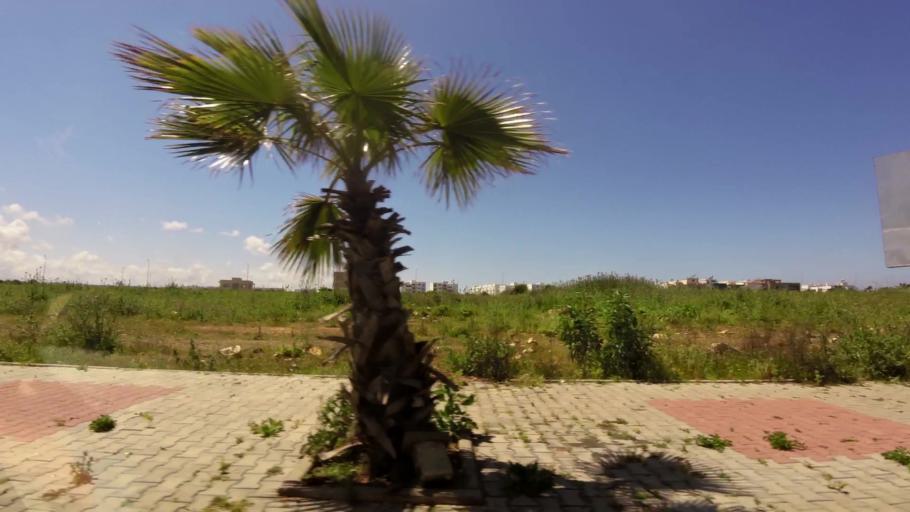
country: MA
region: Grand Casablanca
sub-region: Nouaceur
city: Dar Bouazza
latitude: 33.5256
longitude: -7.8194
